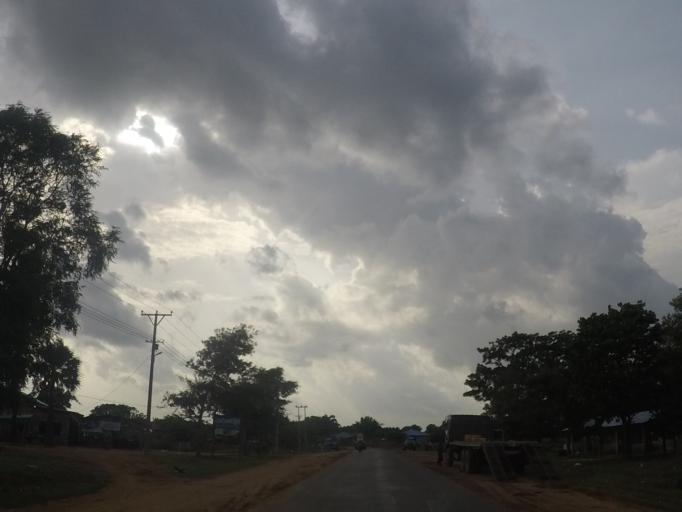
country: MM
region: Mandalay
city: Yamethin
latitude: 20.5039
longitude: 95.7809
